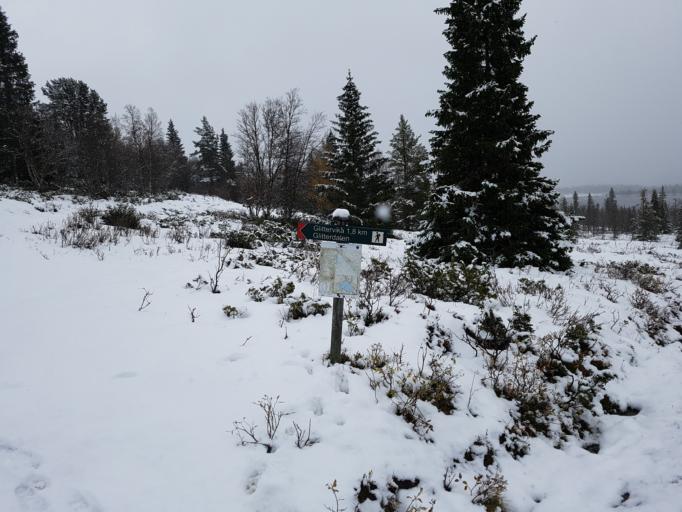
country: NO
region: Oppland
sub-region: Sel
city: Otta
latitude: 61.7971
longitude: 9.7145
